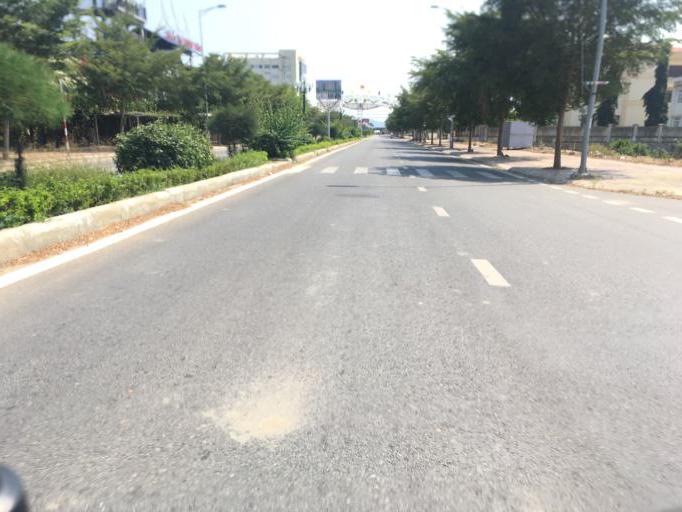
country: VN
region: Ninh Thuan
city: Phan Rang-Thap Cham
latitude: 11.5686
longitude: 109.0013
